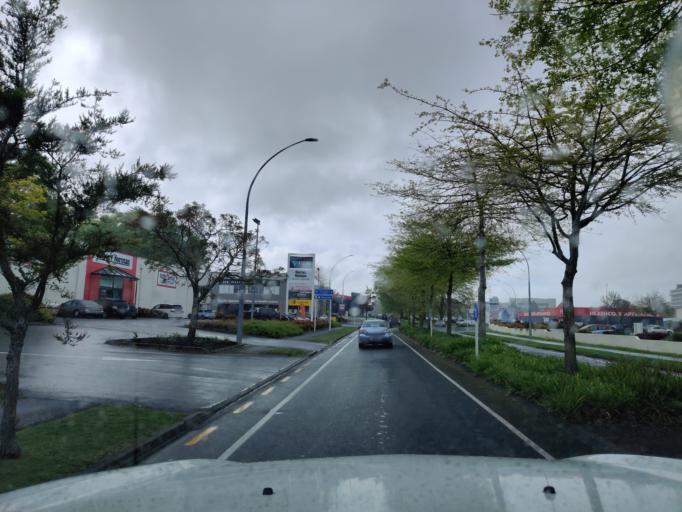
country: NZ
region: Waikato
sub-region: Hamilton City
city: Hamilton
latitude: -37.7934
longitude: 175.2825
